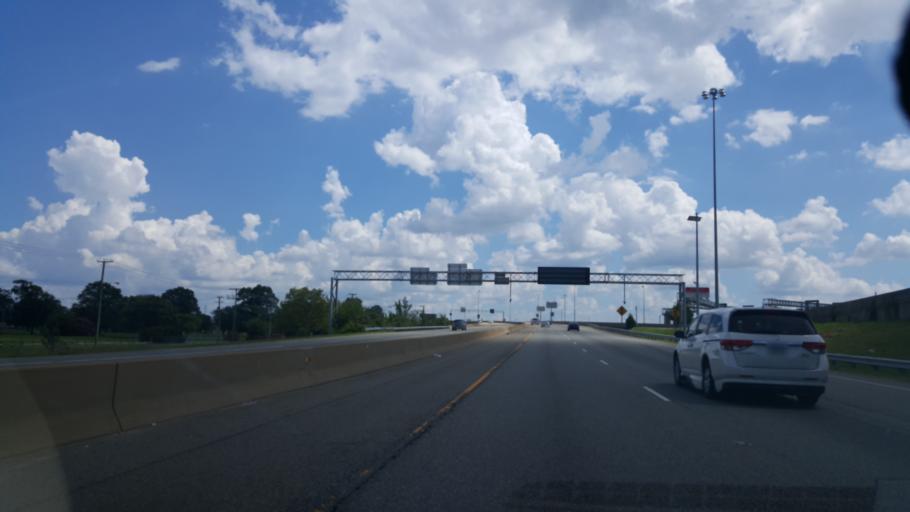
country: US
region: Virginia
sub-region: City of Newport News
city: Newport News
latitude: 36.9788
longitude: -76.4235
